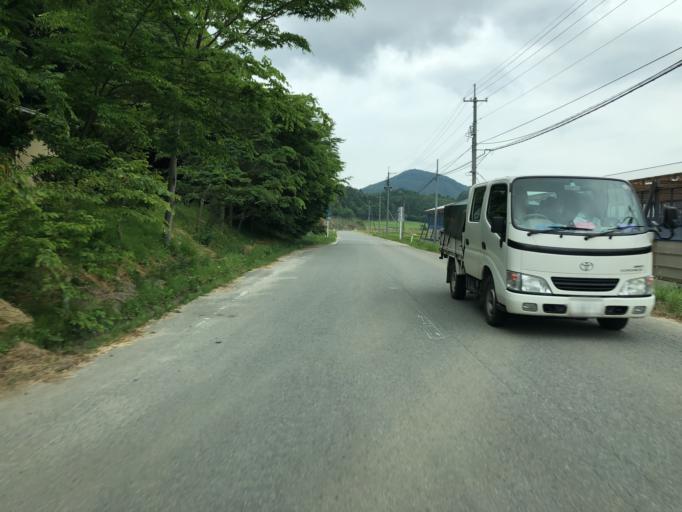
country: JP
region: Fukushima
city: Funehikimachi-funehiki
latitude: 37.3836
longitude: 140.7474
